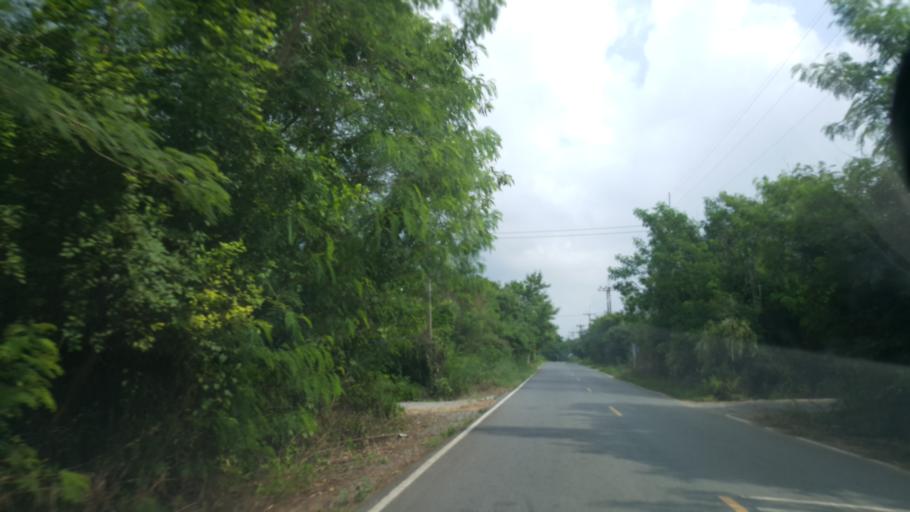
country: TH
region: Chon Buri
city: Sattahip
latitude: 12.7085
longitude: 100.9086
